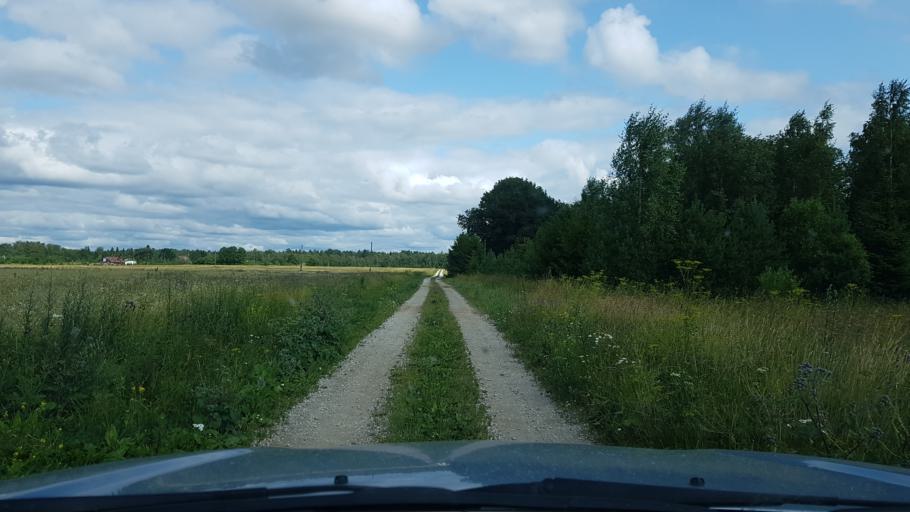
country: EE
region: Ida-Virumaa
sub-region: Narva-Joesuu linn
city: Narva-Joesuu
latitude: 59.3701
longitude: 27.9451
